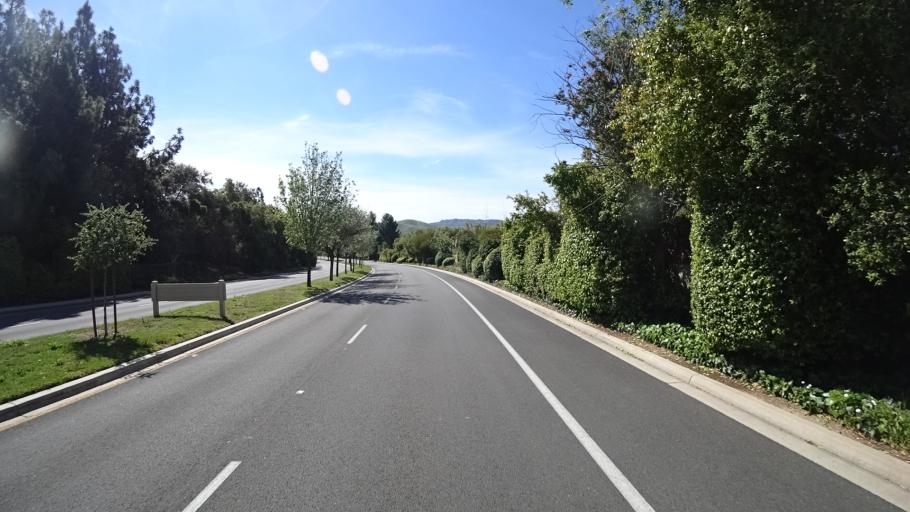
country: US
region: California
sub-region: Ventura County
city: Oak Park
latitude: 34.1881
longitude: -118.7905
